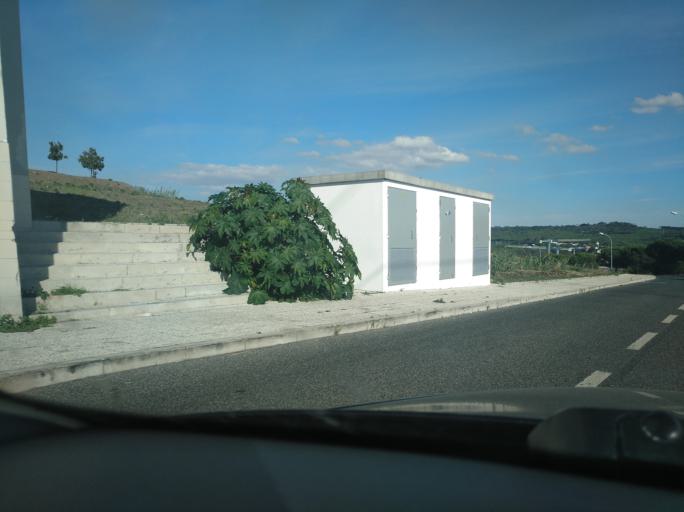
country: PT
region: Lisbon
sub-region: Oeiras
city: Linda-a-Velha
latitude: 38.7171
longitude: -9.2304
